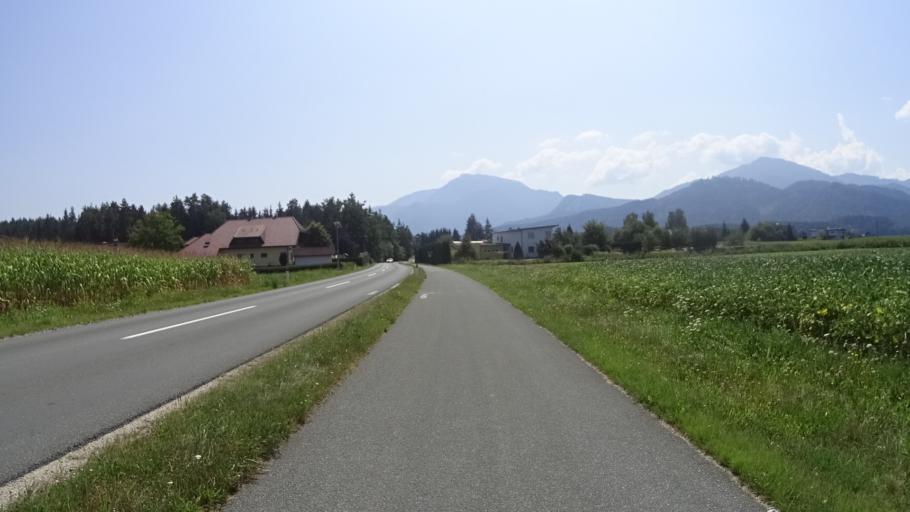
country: AT
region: Carinthia
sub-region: Politischer Bezirk Volkermarkt
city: Eberndorf
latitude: 46.5751
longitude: 14.6566
